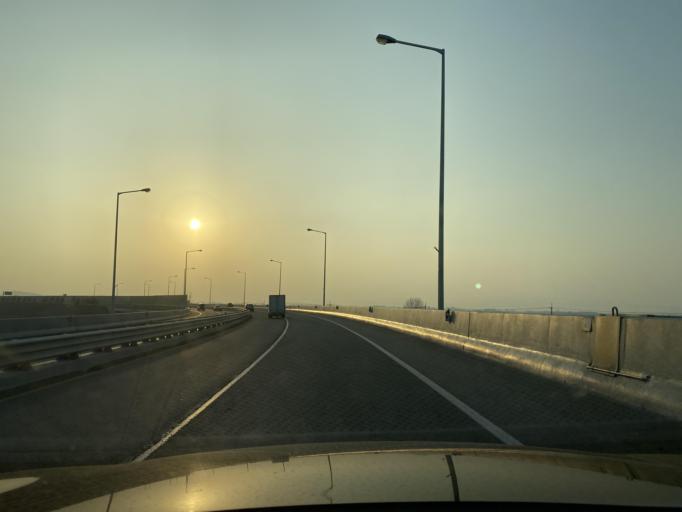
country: KR
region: Chungcheongnam-do
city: Yesan
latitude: 36.7043
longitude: 126.8241
